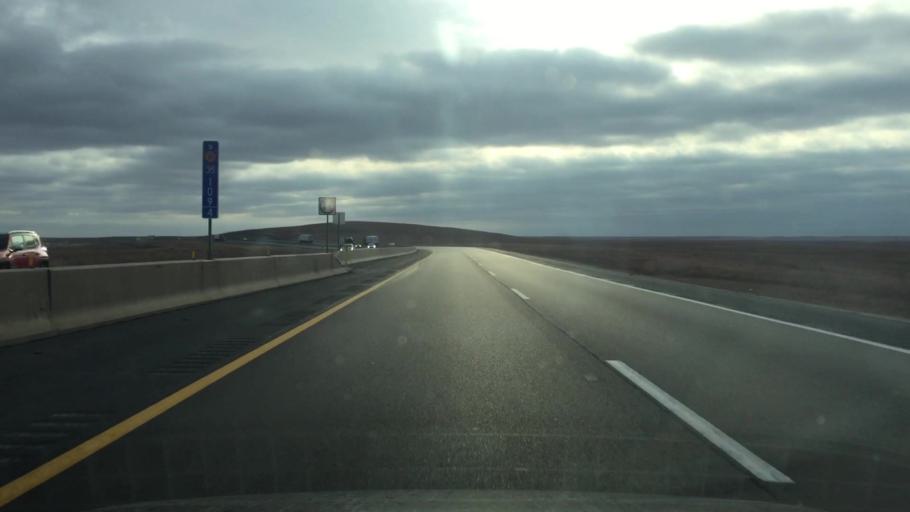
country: US
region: Kansas
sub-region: Chase County
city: Cottonwood Falls
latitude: 38.2206
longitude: -96.4318
